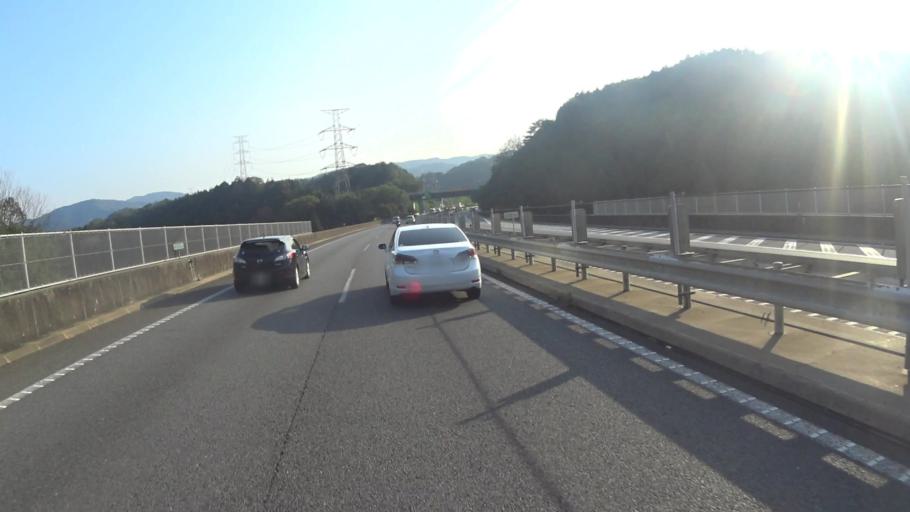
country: JP
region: Shiga Prefecture
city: Otsu-shi
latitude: 34.9230
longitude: 135.8859
